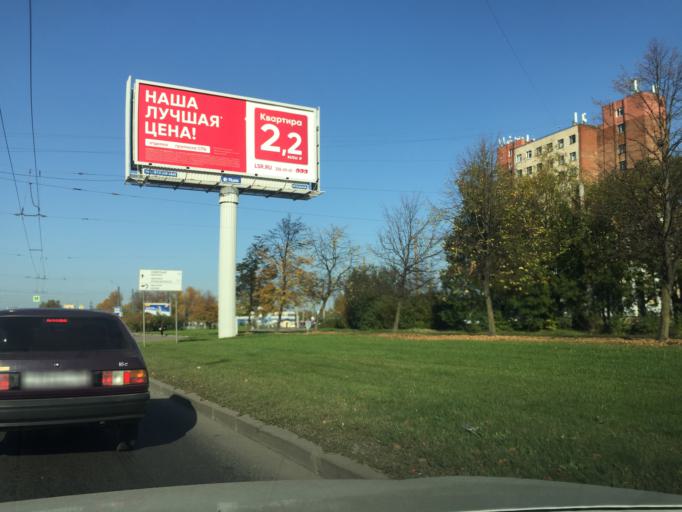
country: RU
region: Leningrad
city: Akademicheskoe
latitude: 60.0020
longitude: 30.4367
